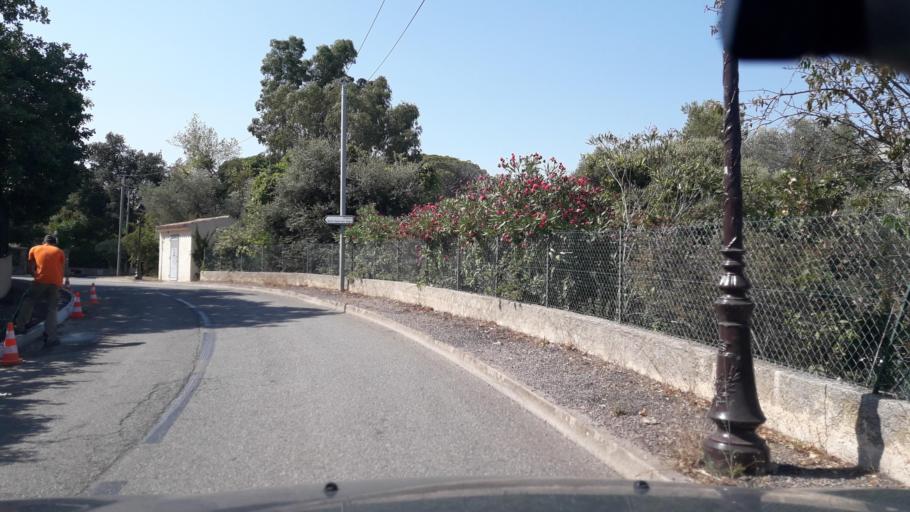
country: FR
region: Provence-Alpes-Cote d'Azur
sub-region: Departement du Var
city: Saint-Raphael
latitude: 43.4548
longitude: 6.7625
